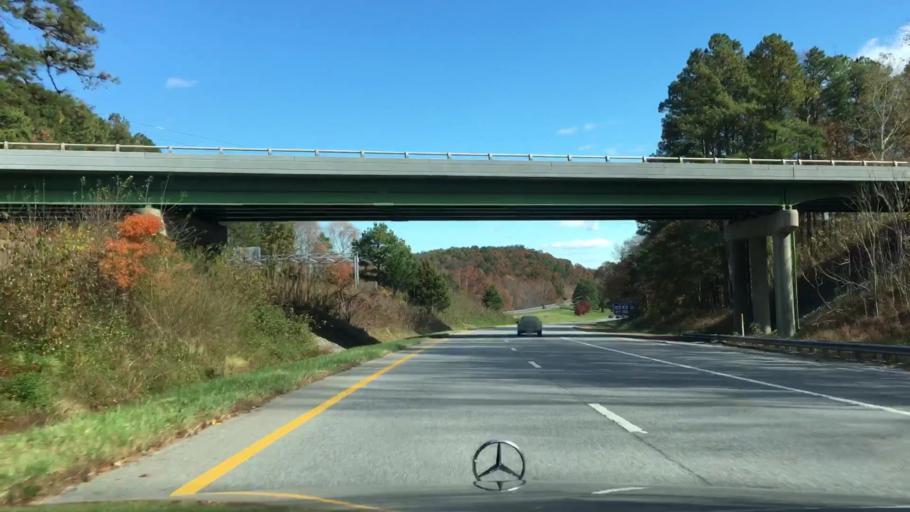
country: US
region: Virginia
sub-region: Campbell County
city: Altavista
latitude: 37.1358
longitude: -79.2905
